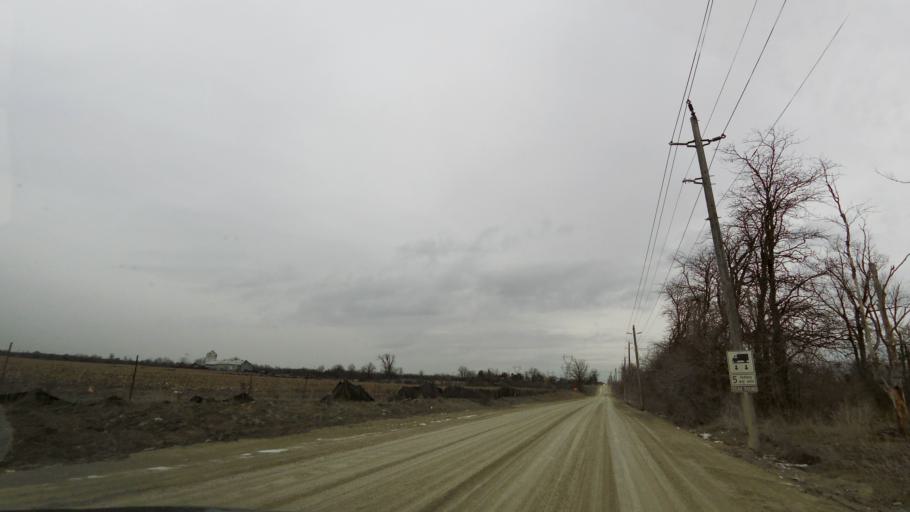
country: CA
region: Ontario
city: Vaughan
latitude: 43.8202
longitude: -79.6590
